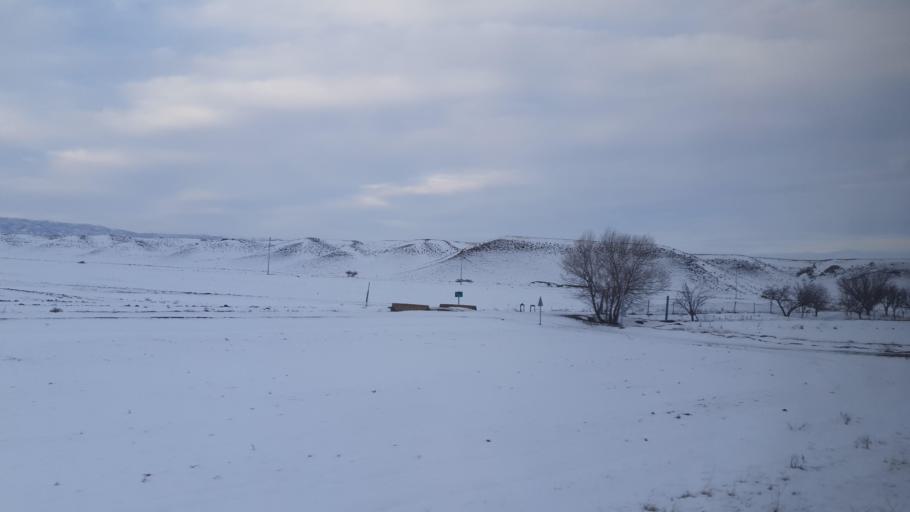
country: TR
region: Kirsehir
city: Mecidiye
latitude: 39.6903
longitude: 34.3868
